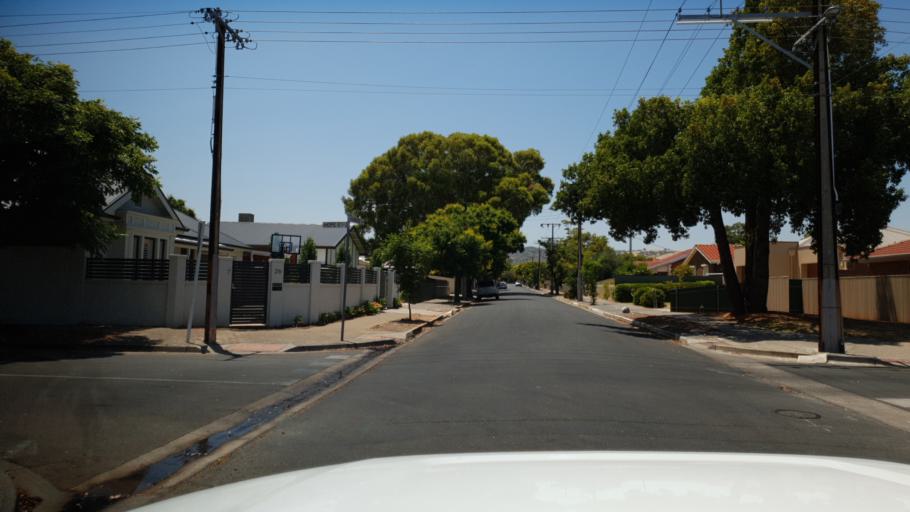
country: AU
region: South Australia
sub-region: Mitcham
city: Clarence Gardens
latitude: -34.9796
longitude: 138.5883
